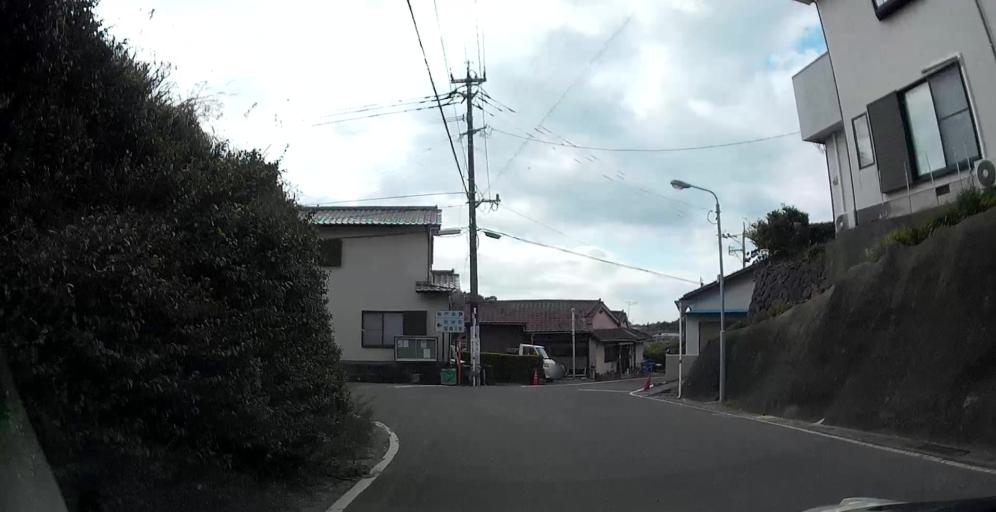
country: JP
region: Kumamoto
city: Minamata
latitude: 32.2093
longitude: 130.3846
